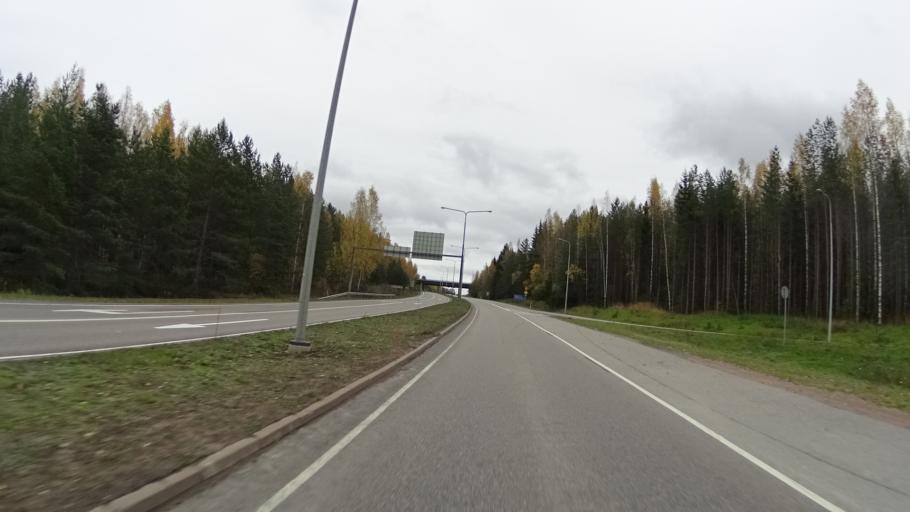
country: FI
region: Kymenlaakso
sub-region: Kouvola
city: Kouvola
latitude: 60.8845
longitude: 26.7669
